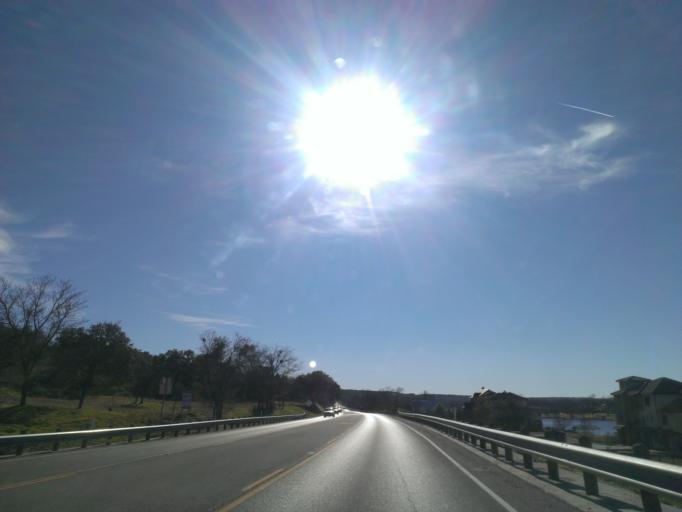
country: US
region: Texas
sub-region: Burnet County
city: Meadowlakes
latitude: 30.5614
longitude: -98.2789
